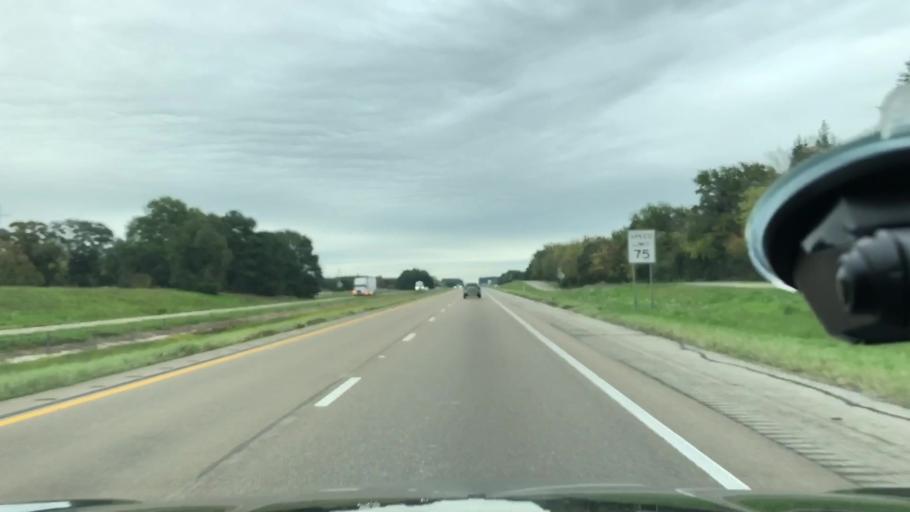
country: US
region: Texas
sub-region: Franklin County
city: Mount Vernon
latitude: 33.1599
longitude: -95.1010
